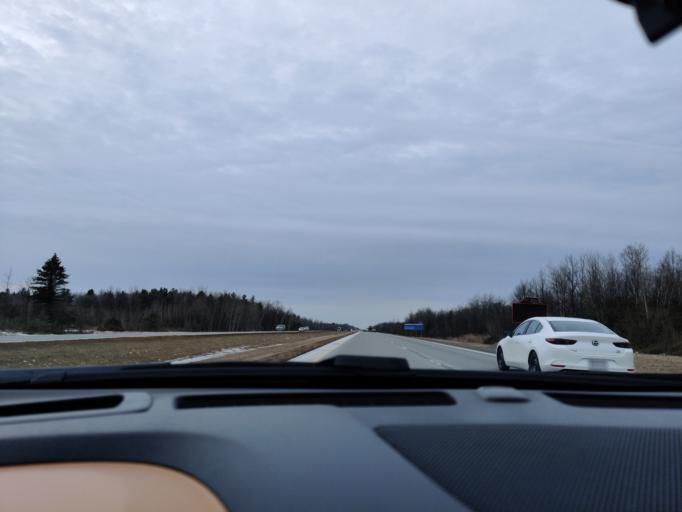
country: US
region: New York
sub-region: St. Lawrence County
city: Ogdensburg
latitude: 44.8251
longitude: -75.3826
